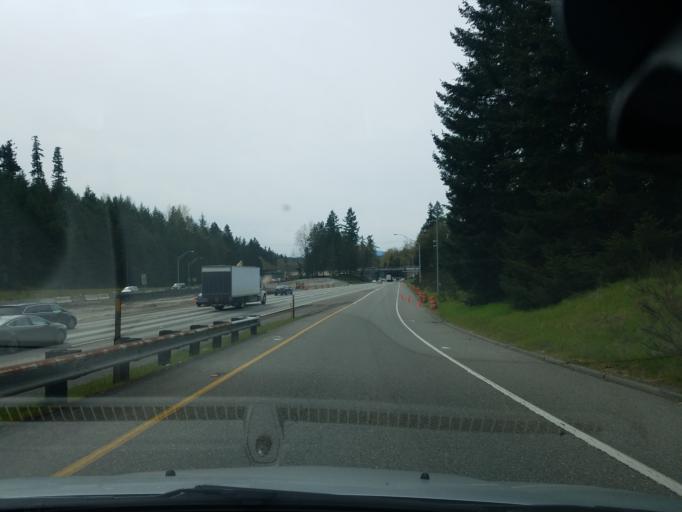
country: US
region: Washington
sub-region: Pierce County
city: DuPont
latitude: 47.0827
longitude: -122.6721
